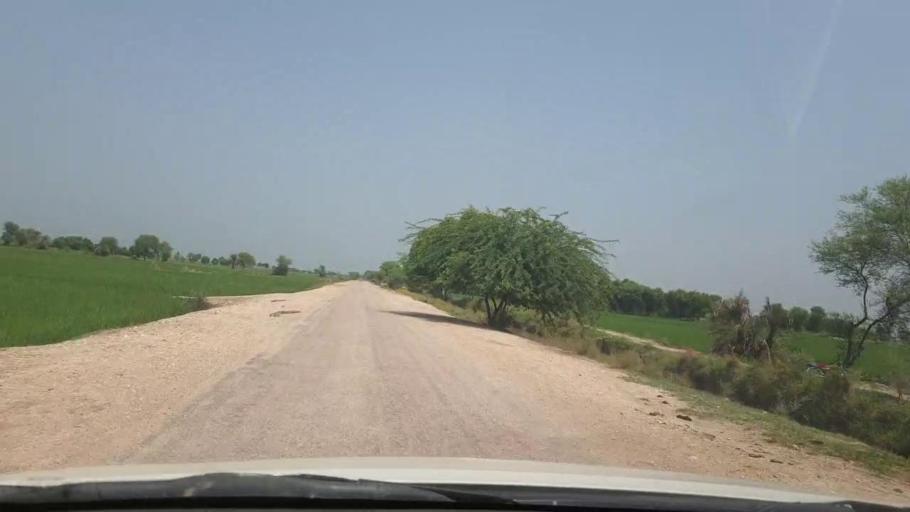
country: PK
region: Sindh
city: Rustam jo Goth
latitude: 28.0278
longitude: 68.7672
